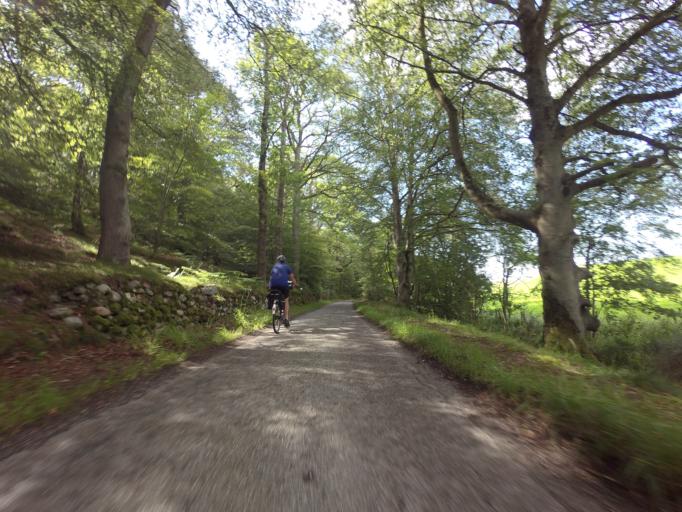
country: GB
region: Scotland
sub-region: Highland
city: Nairn
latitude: 57.5456
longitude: -3.8613
